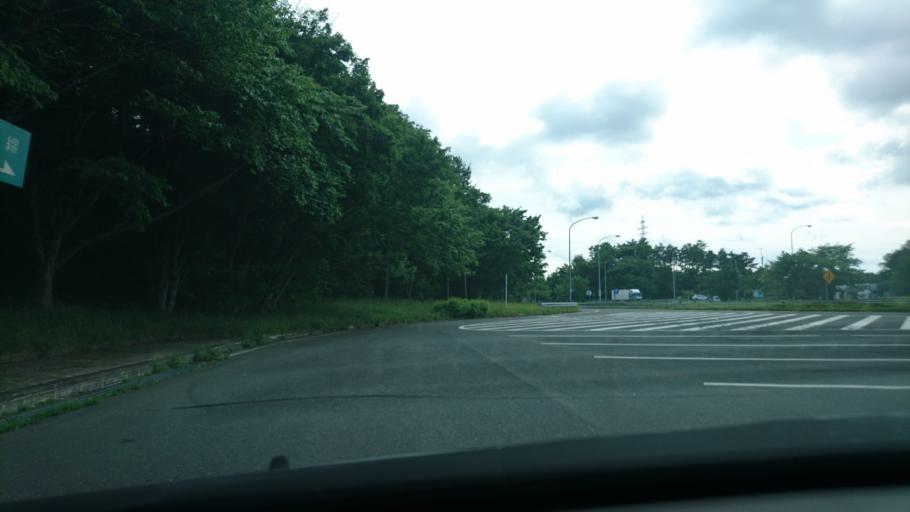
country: JP
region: Aomori
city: Hachinohe
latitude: 40.4444
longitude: 141.4503
